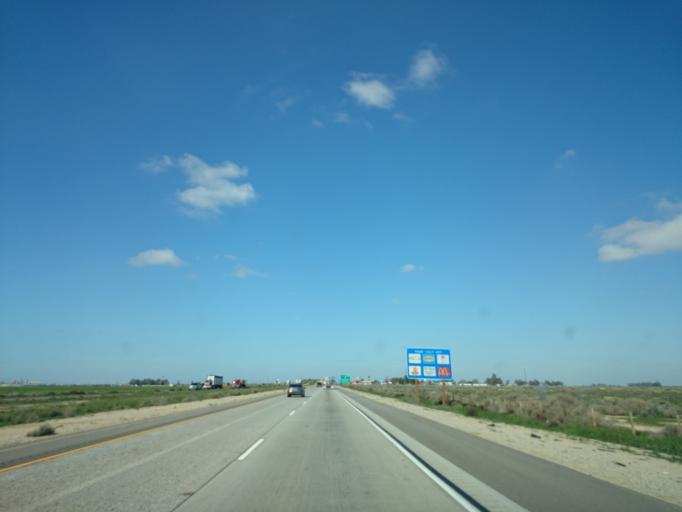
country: US
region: California
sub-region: Kern County
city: Buttonwillow
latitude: 35.3917
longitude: -119.3872
